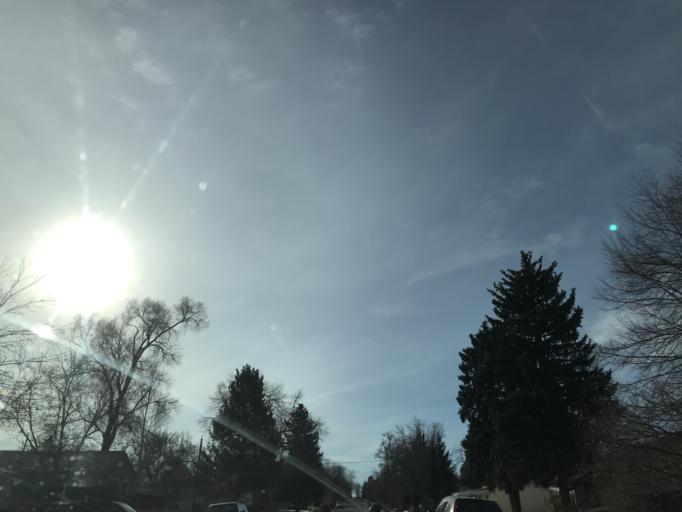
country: US
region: Colorado
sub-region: Arapahoe County
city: Littleton
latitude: 39.6012
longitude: -105.0093
